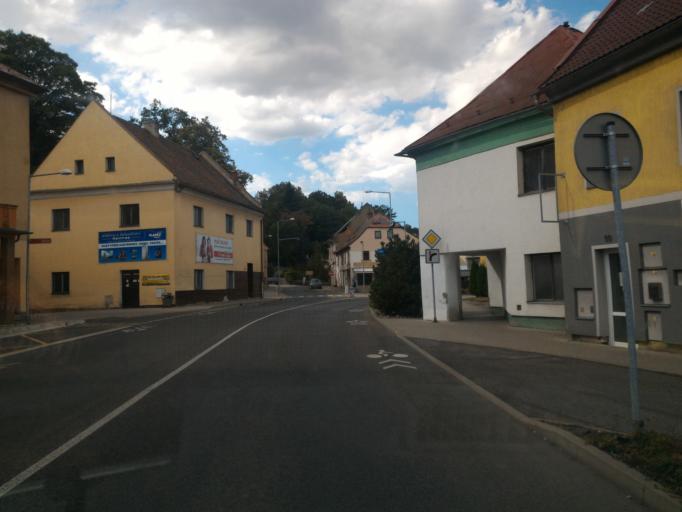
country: CZ
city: Mimon
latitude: 50.6551
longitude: 14.7255
